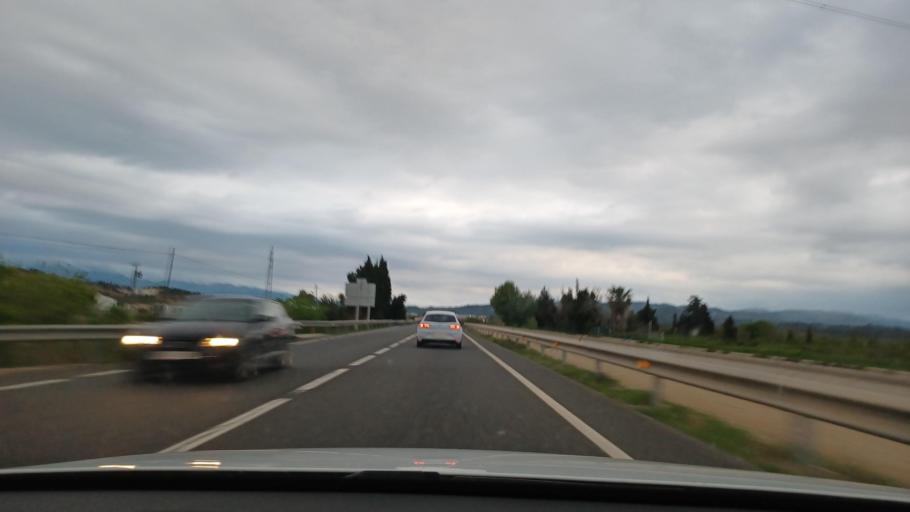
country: ES
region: Catalonia
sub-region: Provincia de Tarragona
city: Amposta
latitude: 40.7305
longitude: 0.5701
